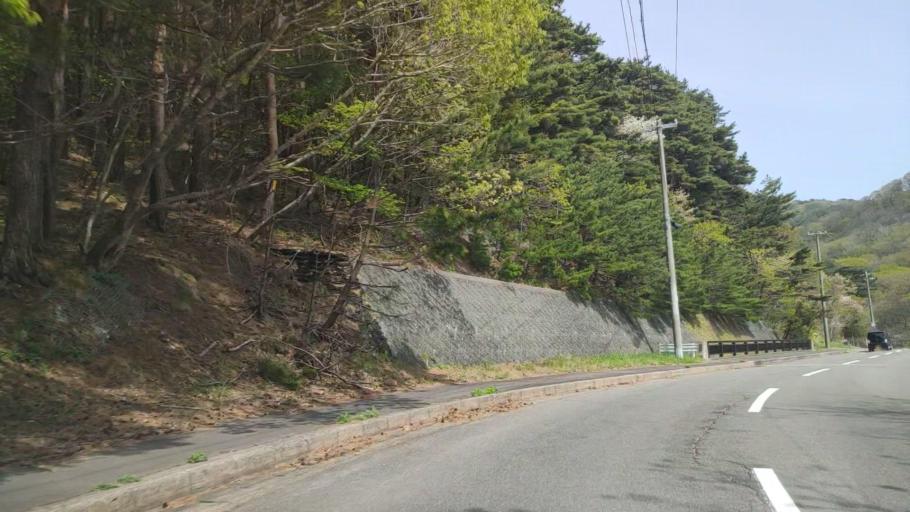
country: JP
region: Aomori
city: Aomori Shi
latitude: 40.9018
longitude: 140.8628
